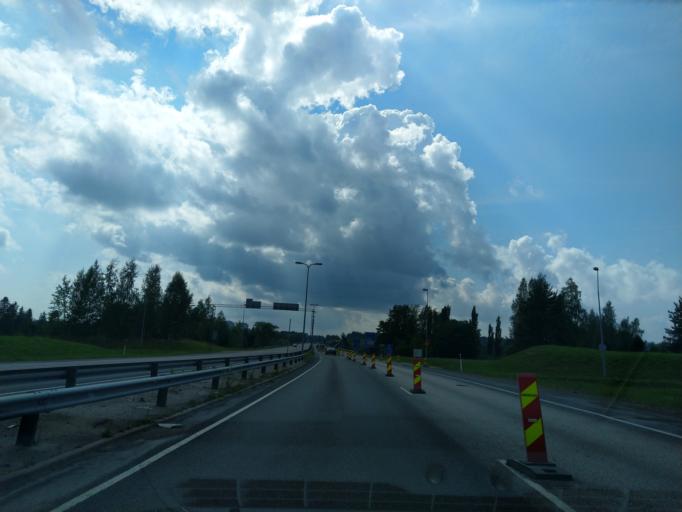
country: FI
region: South Karelia
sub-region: Imatra
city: Imatra
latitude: 61.1982
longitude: 28.7886
